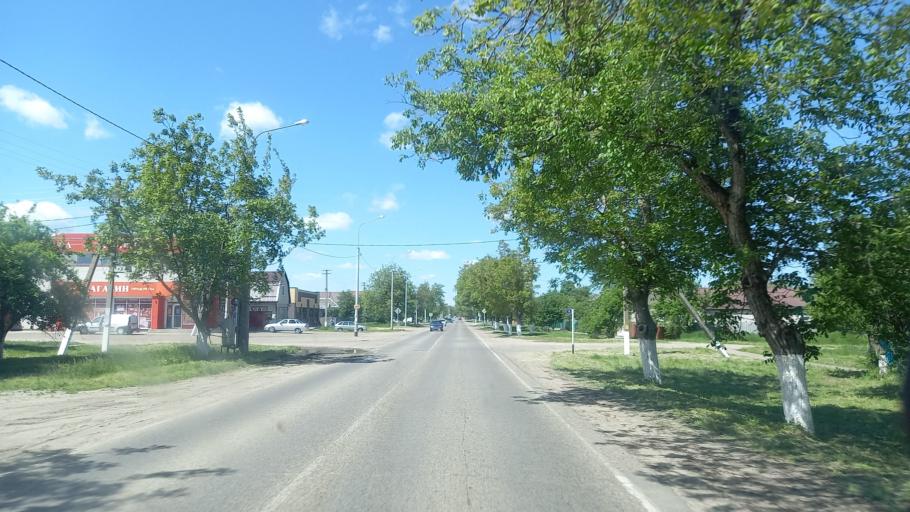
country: RU
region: Krasnodarskiy
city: Novoukrainskoye
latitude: 45.3804
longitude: 40.5174
